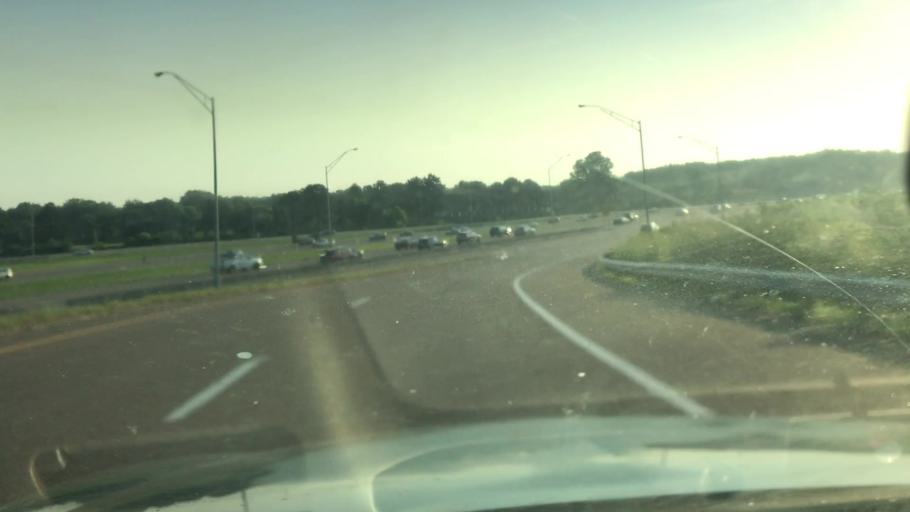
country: US
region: Tennessee
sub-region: Shelby County
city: New South Memphis
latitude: 35.0802
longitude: -89.9528
